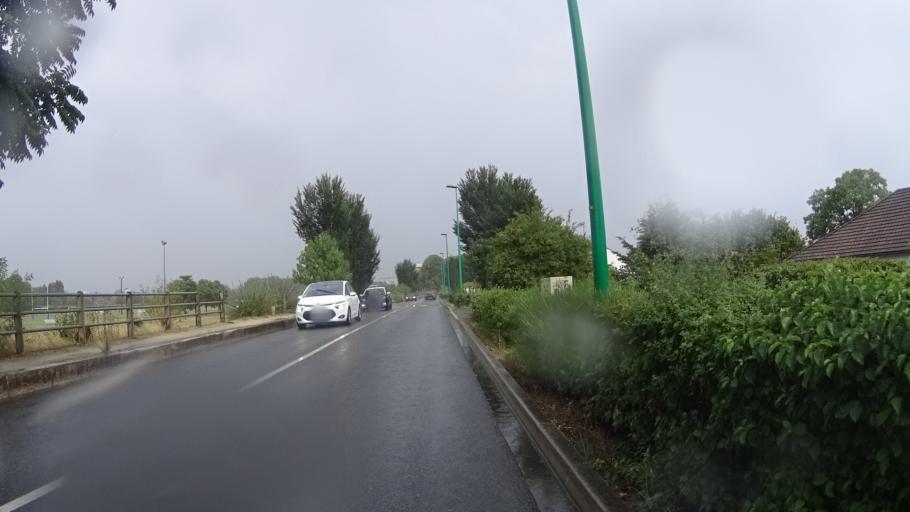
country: FR
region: Centre
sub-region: Departement du Loiret
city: Saint-Pryve-Saint-Mesmin
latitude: 47.8925
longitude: 1.8815
